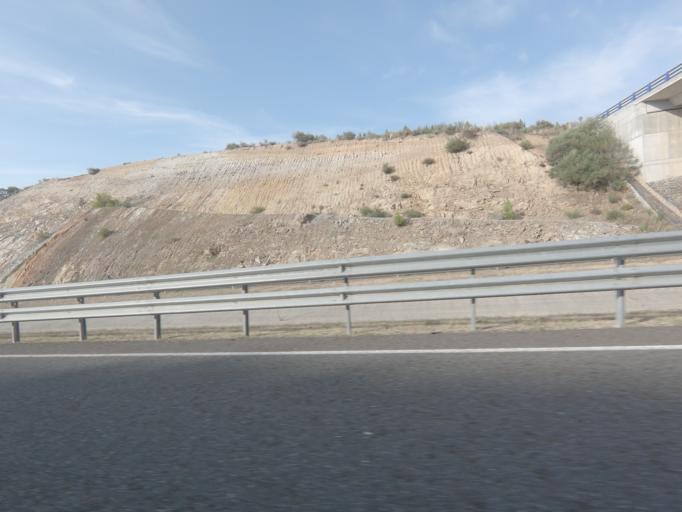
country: ES
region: Galicia
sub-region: Provincia de Ourense
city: Oimbra
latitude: 41.8564
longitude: -7.4233
